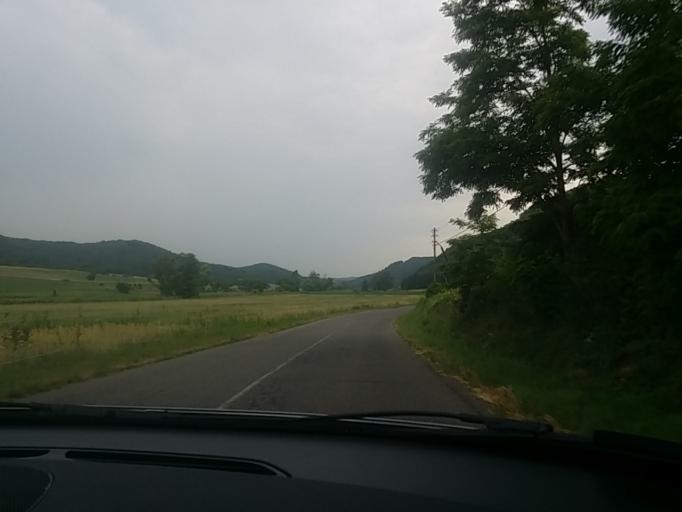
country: HU
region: Borsod-Abauj-Zemplen
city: Arlo
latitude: 48.2206
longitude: 20.1803
